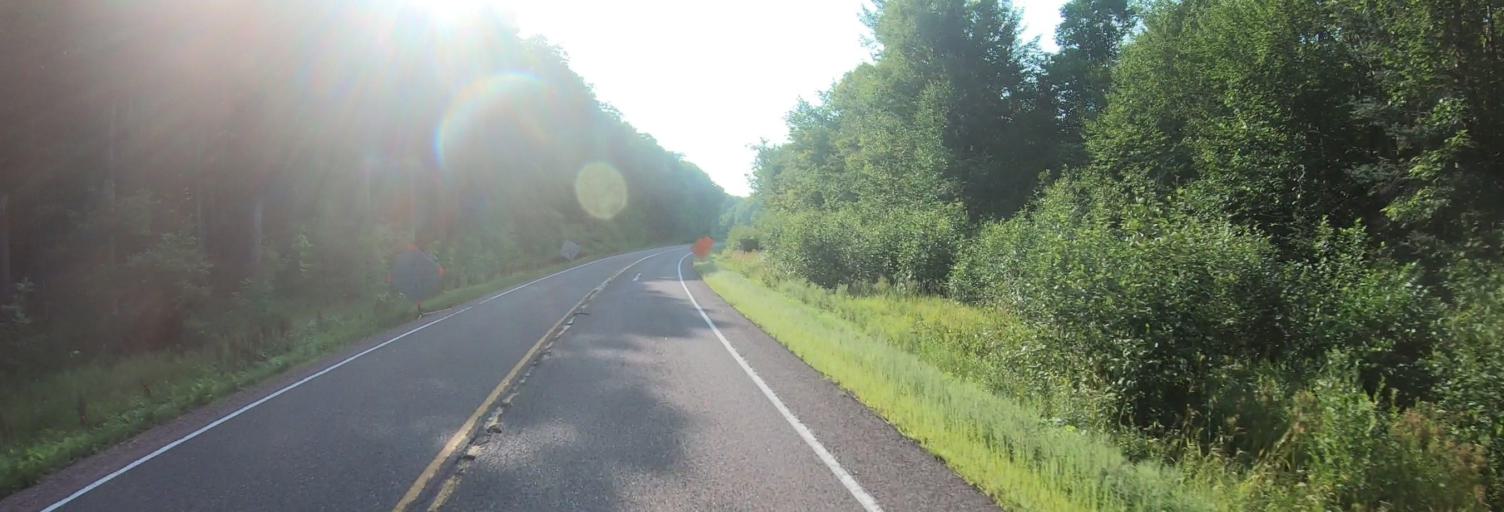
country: US
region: Wisconsin
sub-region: Ashland County
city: Ashland
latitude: 46.3098
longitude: -90.7387
